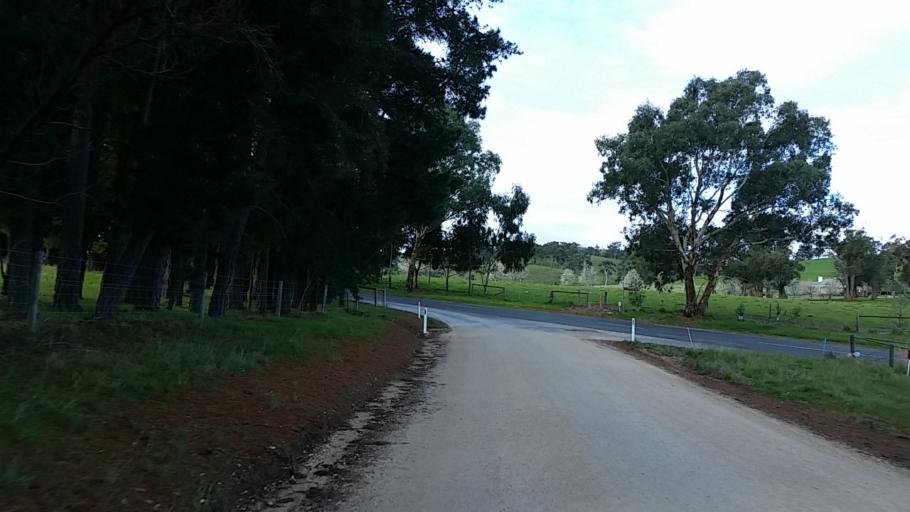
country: AU
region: South Australia
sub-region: Mount Barker
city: Hahndorf
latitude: -35.0133
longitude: 138.8239
